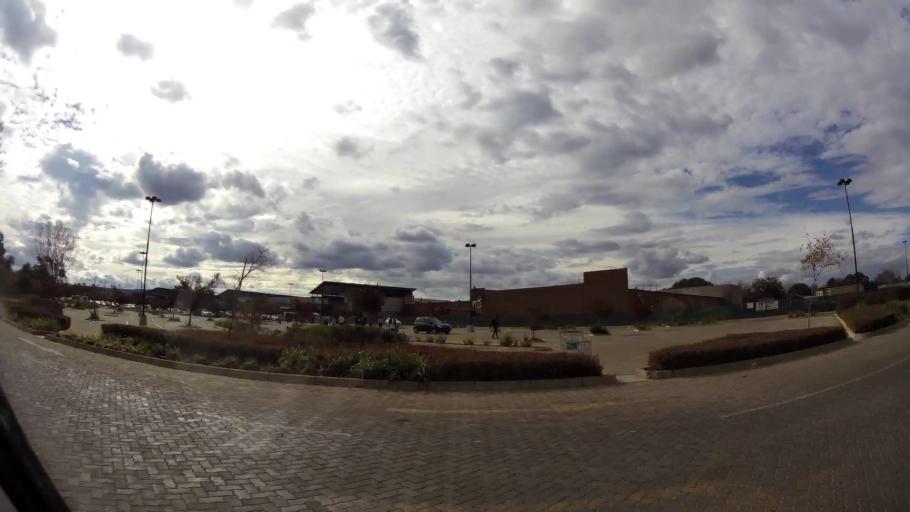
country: ZA
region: Limpopo
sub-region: Waterberg District Municipality
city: Modimolle
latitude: -24.6979
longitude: 28.4071
